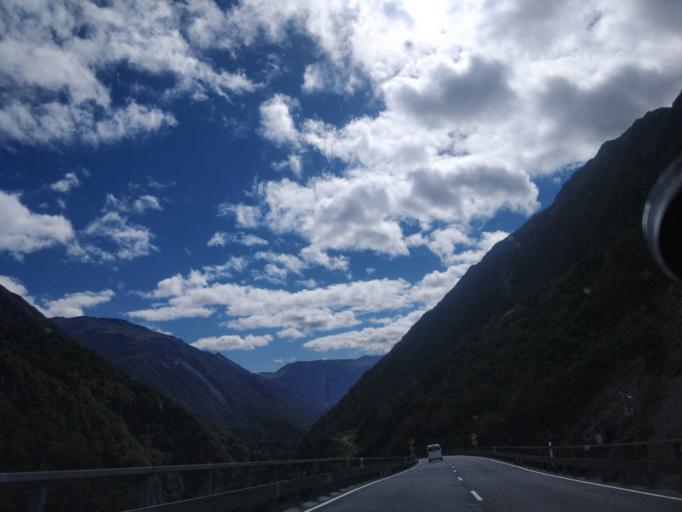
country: NZ
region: West Coast
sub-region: Grey District
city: Greymouth
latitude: -42.8863
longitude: 171.5556
